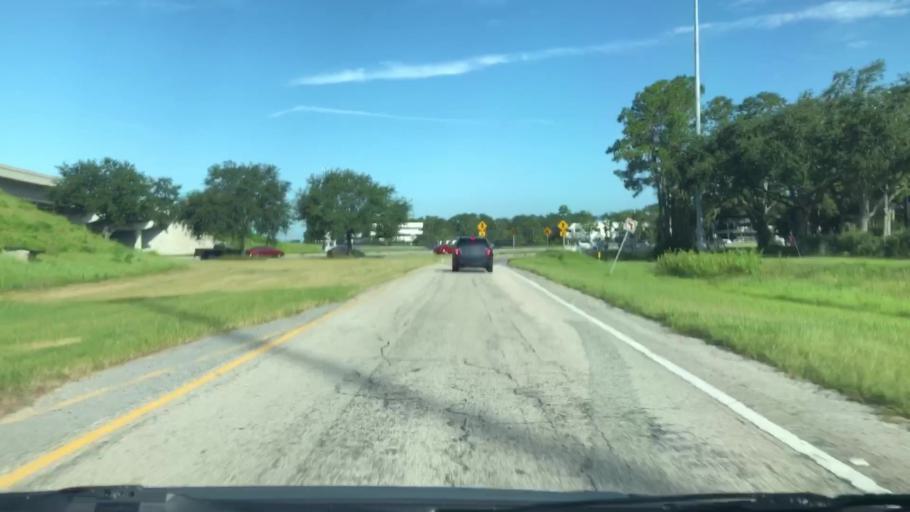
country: US
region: Florida
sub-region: Saint Johns County
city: Fruit Cove
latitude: 30.1816
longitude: -81.6274
